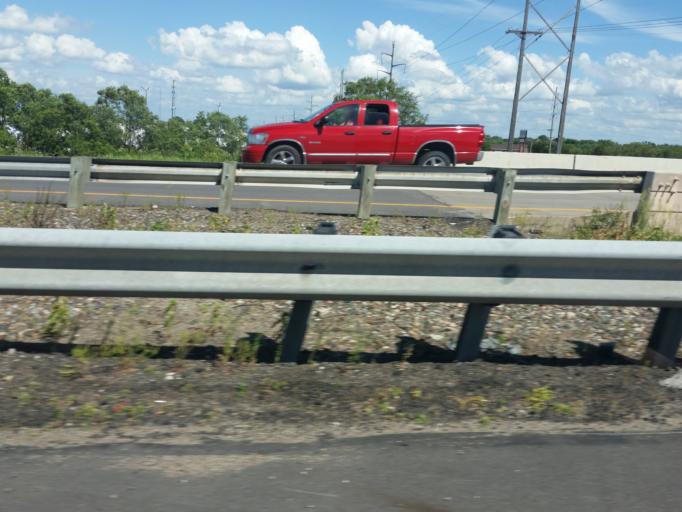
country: US
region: Minnesota
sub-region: Stearns County
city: Waite Park
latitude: 45.5625
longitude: -94.2061
